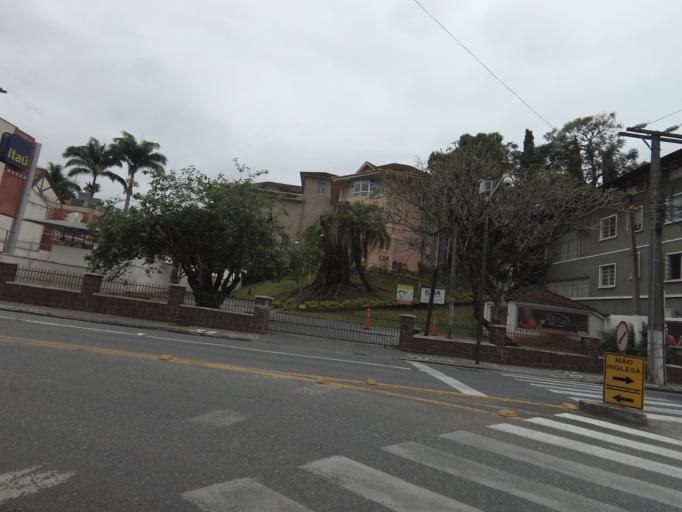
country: BR
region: Santa Catarina
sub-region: Blumenau
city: Blumenau
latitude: -26.9172
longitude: -49.0692
